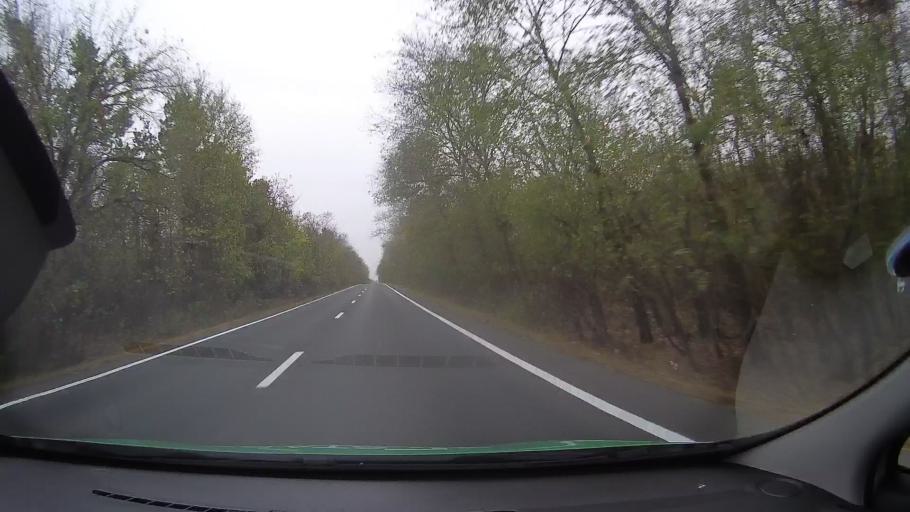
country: RO
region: Ialomita
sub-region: Comuna Mihail Kogalniceanu
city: Mihail Kogalniceanu
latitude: 44.6752
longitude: 27.7635
